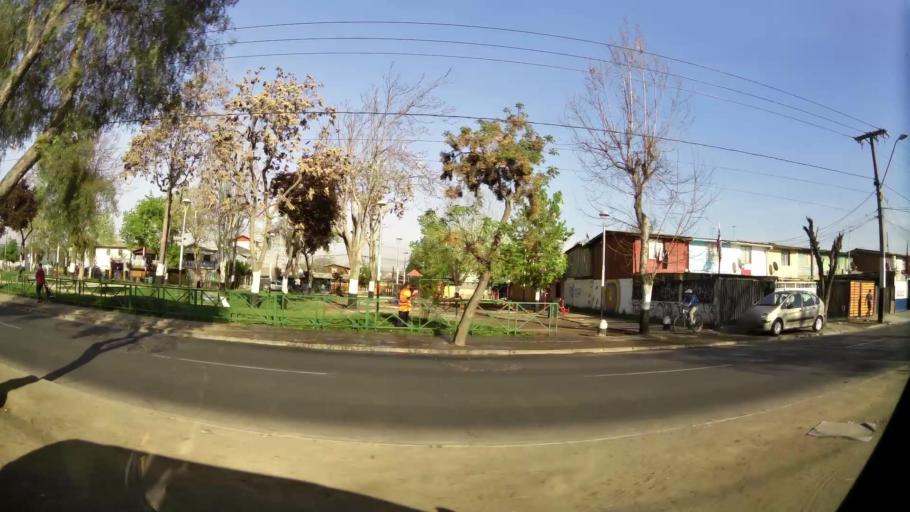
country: CL
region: Santiago Metropolitan
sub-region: Provincia de Santiago
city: Lo Prado
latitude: -33.4355
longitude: -70.7409
